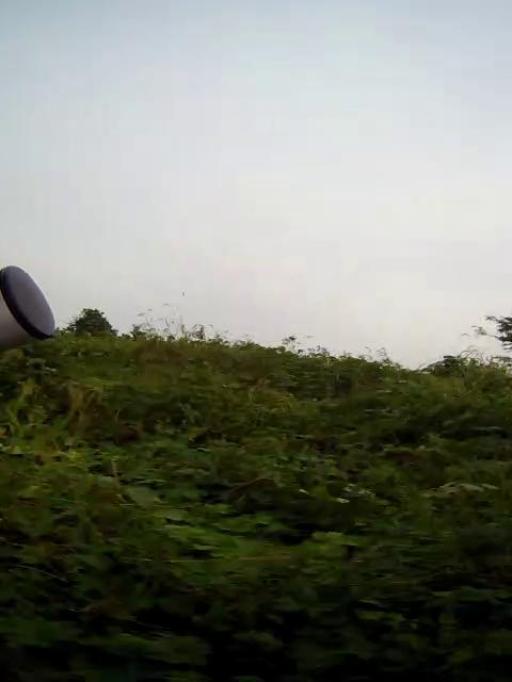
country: JP
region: Hyogo
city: Fukura
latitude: 34.3009
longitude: 134.7898
